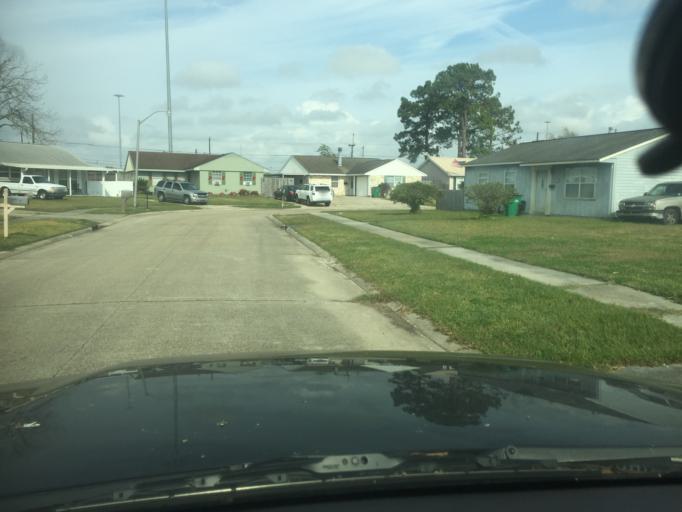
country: US
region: Louisiana
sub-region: Jefferson Parish
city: Avondale
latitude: 29.9158
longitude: -90.2035
